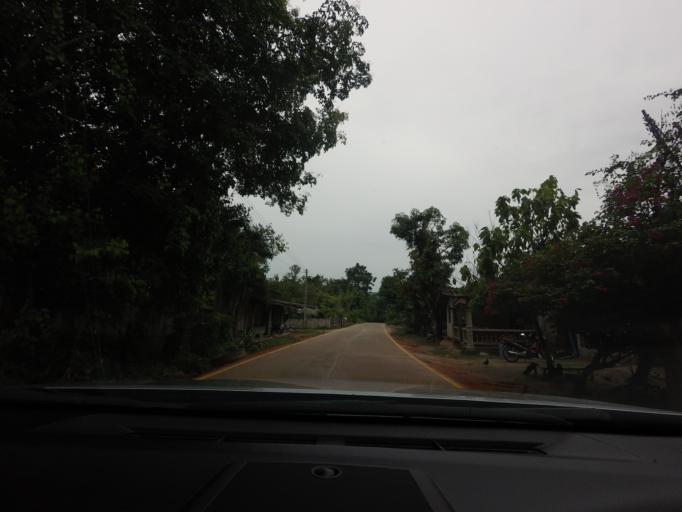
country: TH
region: Narathiwat
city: Rueso
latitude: 6.4082
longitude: 101.5275
